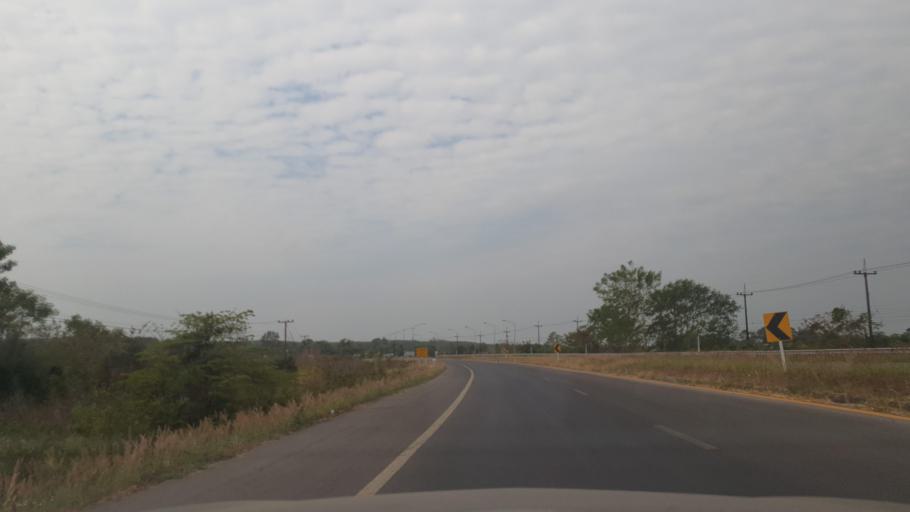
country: TH
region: Changwat Bueng Kan
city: Bung Khla
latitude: 18.3056
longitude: 103.9715
